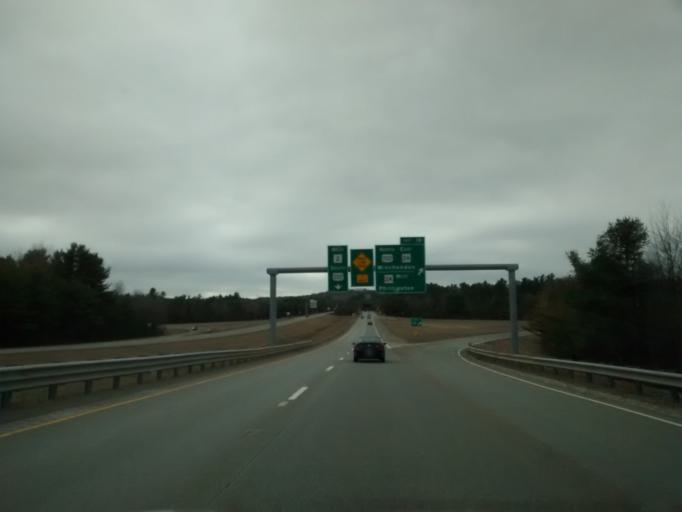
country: US
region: Massachusetts
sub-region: Worcester County
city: Phillipston
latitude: 42.5701
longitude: -72.1219
